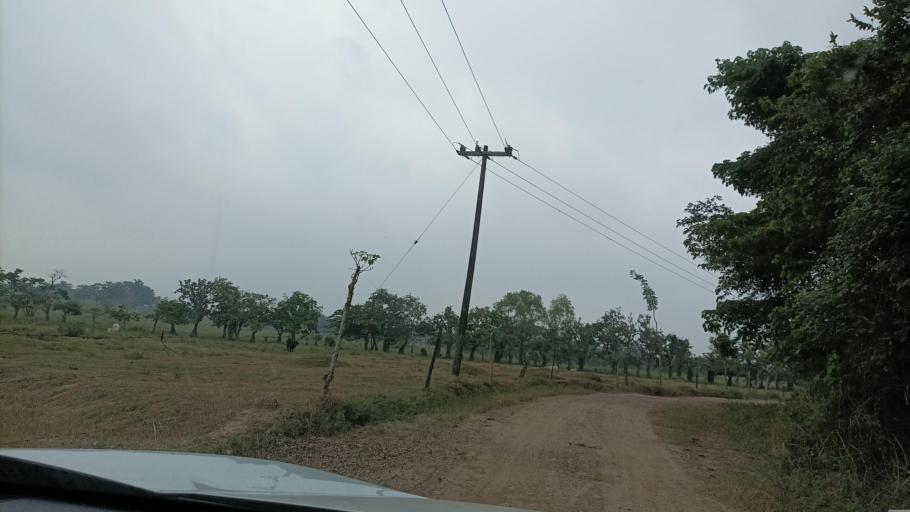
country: MX
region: Veracruz
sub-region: Uxpanapa
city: Poblado 10
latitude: 17.5564
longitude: -94.2263
